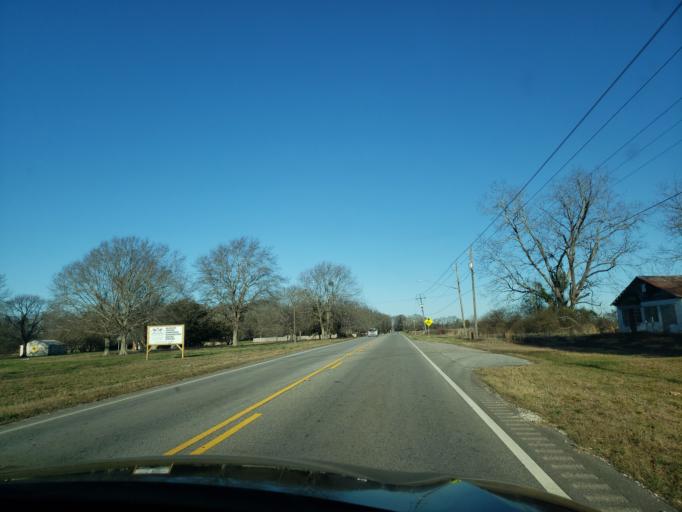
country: US
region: Alabama
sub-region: Lee County
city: Auburn
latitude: 32.6005
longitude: -85.5810
